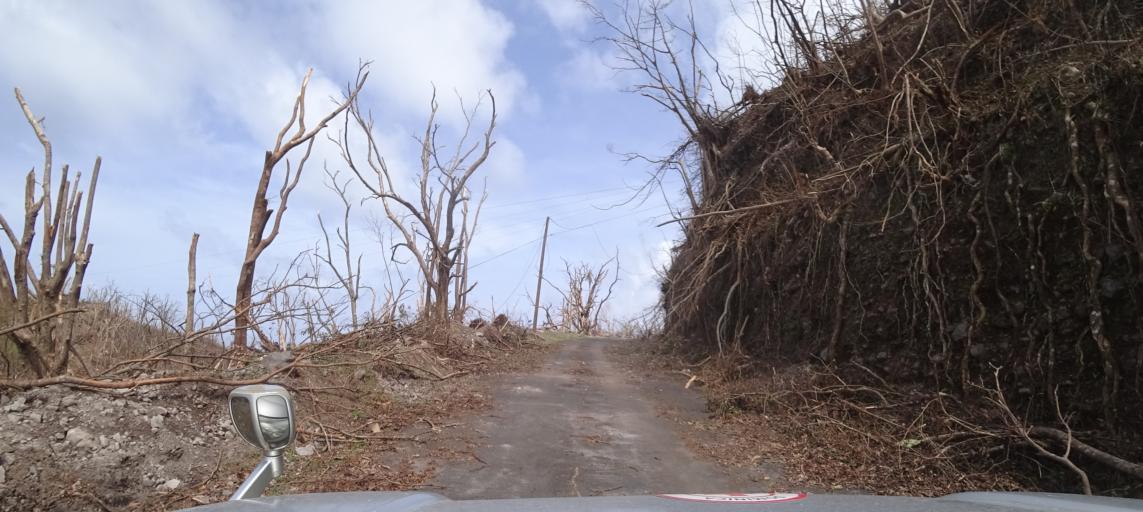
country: DM
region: Saint Patrick
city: La Plaine
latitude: 15.3139
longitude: -61.2496
